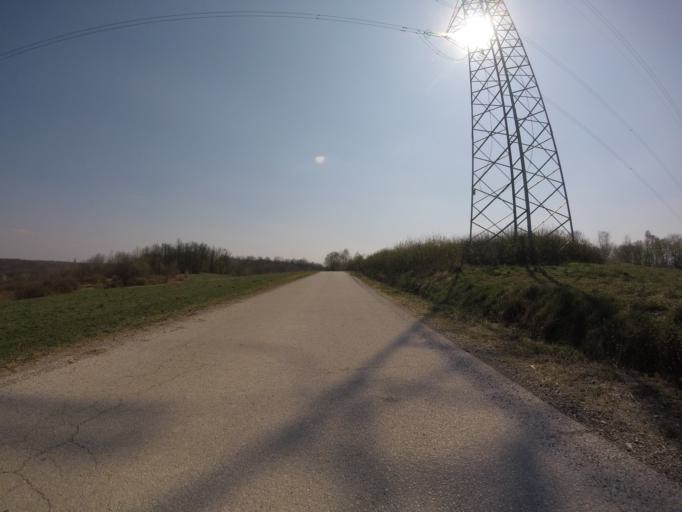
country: HR
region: Grad Zagreb
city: Strmec
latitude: 45.5510
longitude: 15.9020
